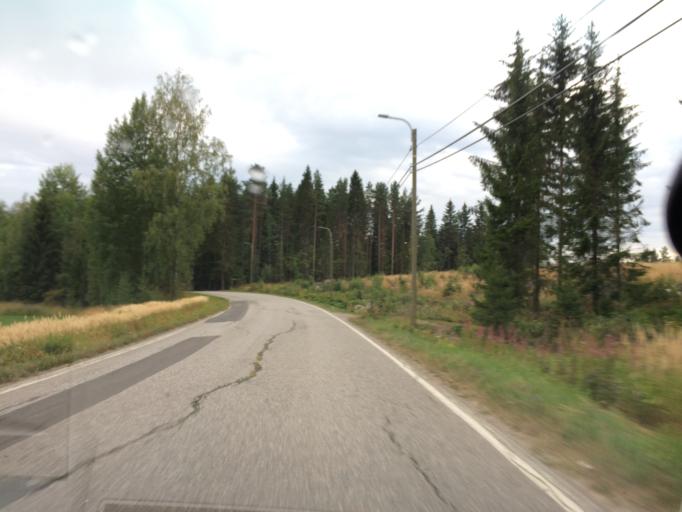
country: FI
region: Haeme
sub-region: Haemeenlinna
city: Tuulos
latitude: 61.1794
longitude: 24.7581
